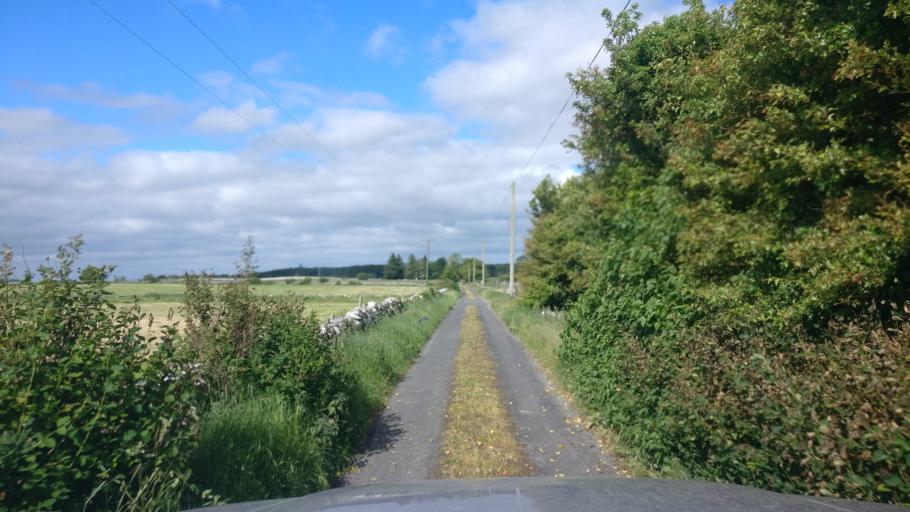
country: IE
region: Connaught
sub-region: County Galway
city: Loughrea
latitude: 53.2349
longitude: -8.6122
